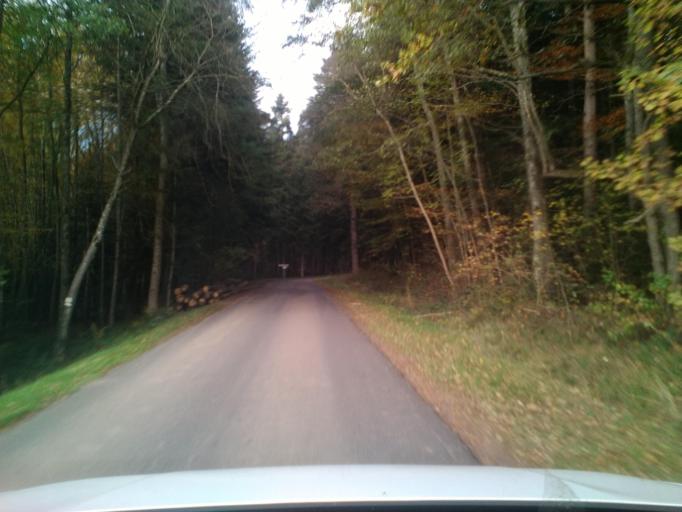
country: FR
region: Lorraine
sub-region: Departement des Vosges
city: Moyenmoutier
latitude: 48.3572
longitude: 6.9275
